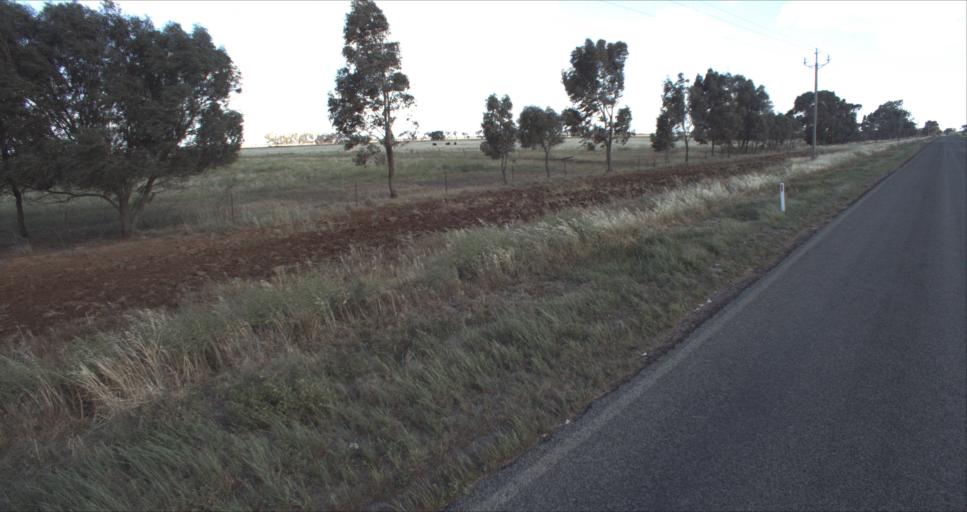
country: AU
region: New South Wales
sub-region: Leeton
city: Leeton
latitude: -34.5319
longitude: 146.2813
